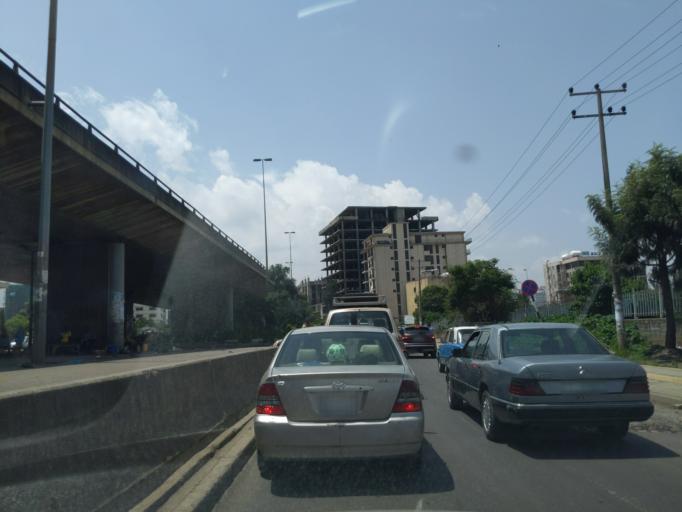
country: ET
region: Adis Abeba
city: Addis Ababa
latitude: 8.9888
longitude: 38.7931
